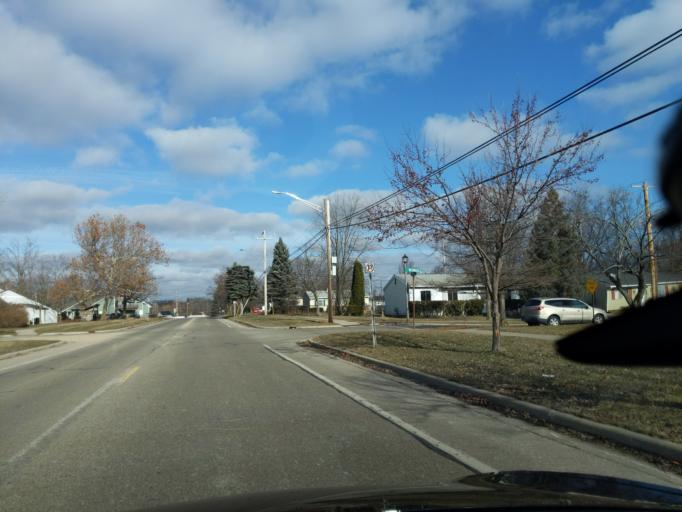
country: US
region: Michigan
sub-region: Ingham County
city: Lansing
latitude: 42.6752
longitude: -84.5727
